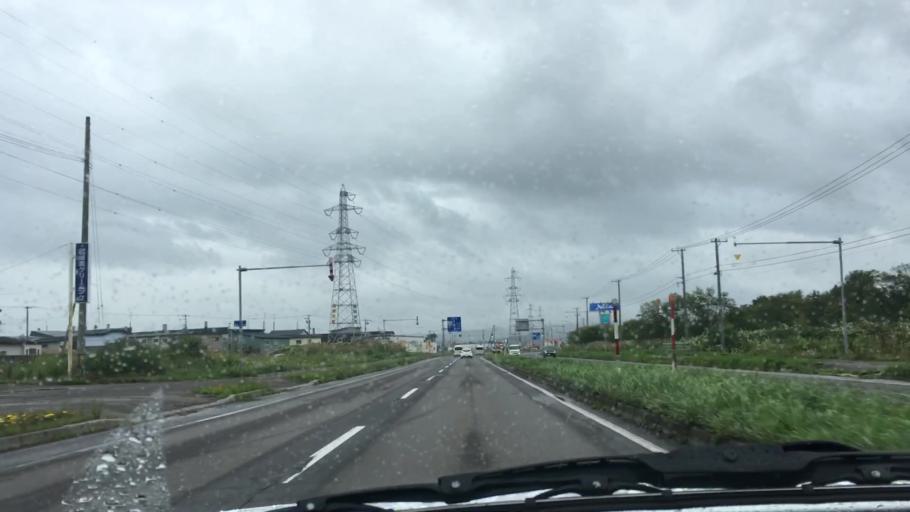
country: JP
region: Hokkaido
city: Nanae
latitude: 42.2558
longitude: 140.2812
